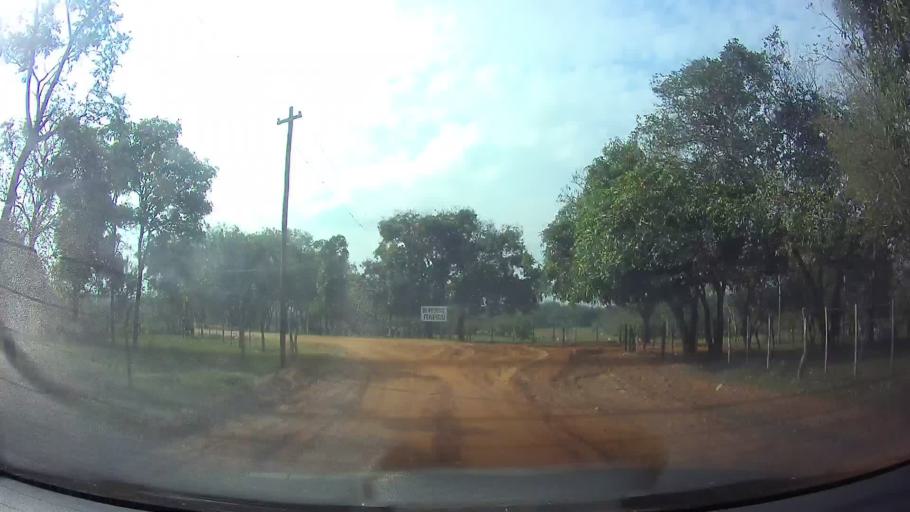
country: PY
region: Cordillera
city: Arroyos y Esteros
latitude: -25.0102
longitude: -57.1982
